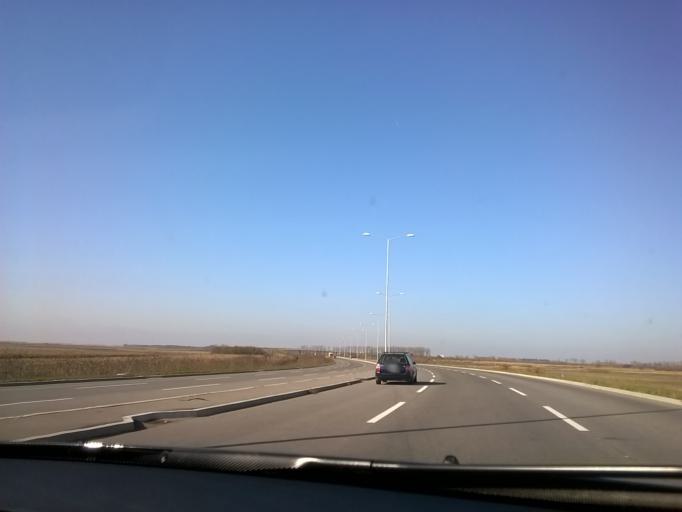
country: RS
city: Ovca
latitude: 44.9124
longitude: 20.5078
